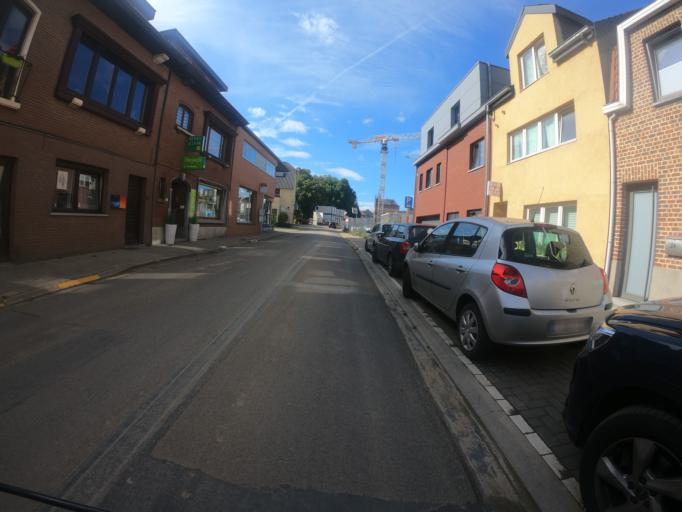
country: BE
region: Flanders
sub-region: Provincie Vlaams-Brabant
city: Wezembeek-Oppem
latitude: 50.8435
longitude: 4.4874
